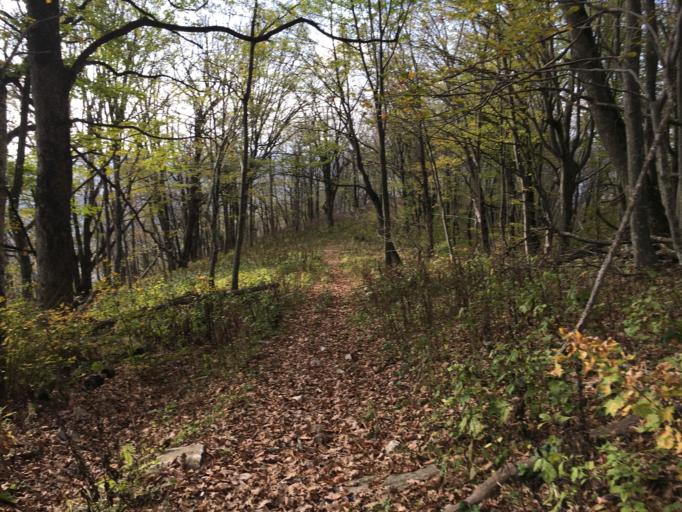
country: RU
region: Krasnodarskiy
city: Nebug
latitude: 44.2425
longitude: 38.9891
